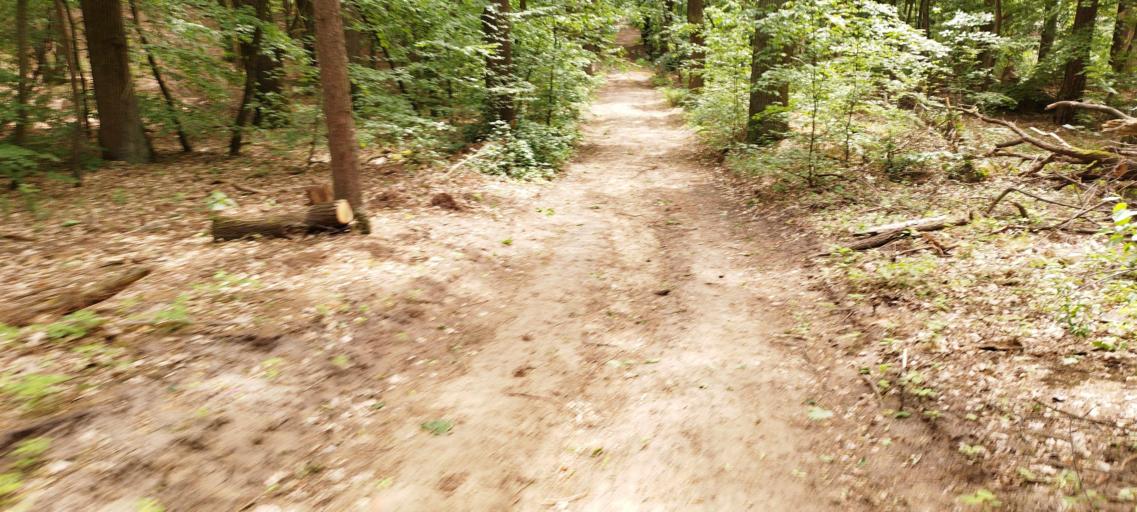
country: DE
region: Brandenburg
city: Rauen
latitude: 52.3216
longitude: 14.0343
